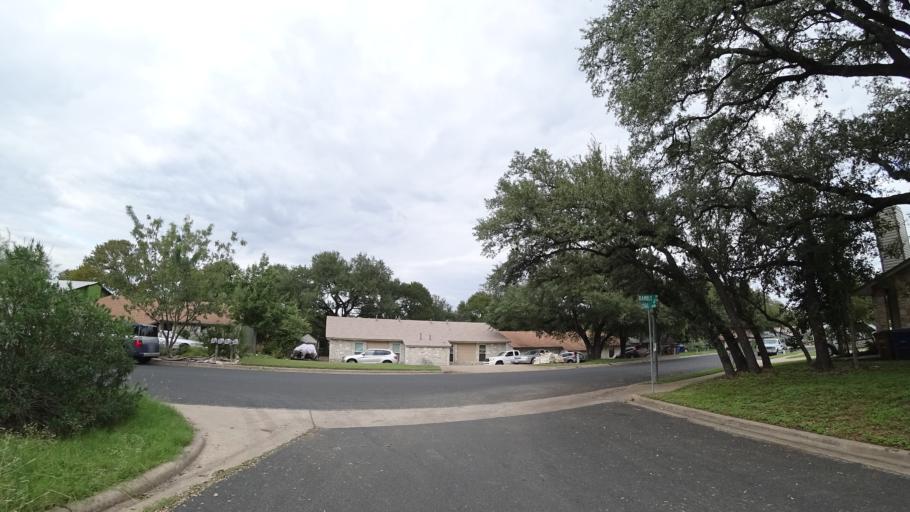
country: US
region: Texas
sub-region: Travis County
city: Rollingwood
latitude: 30.2112
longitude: -97.7811
